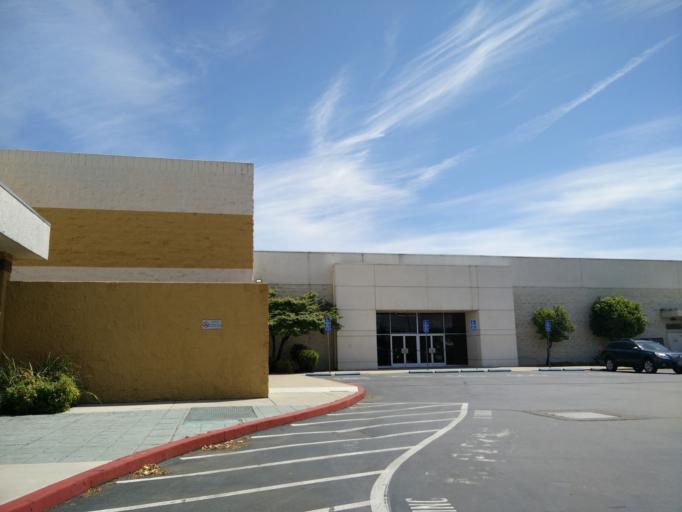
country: US
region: California
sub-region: Shasta County
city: Redding
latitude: 40.5887
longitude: -122.3564
